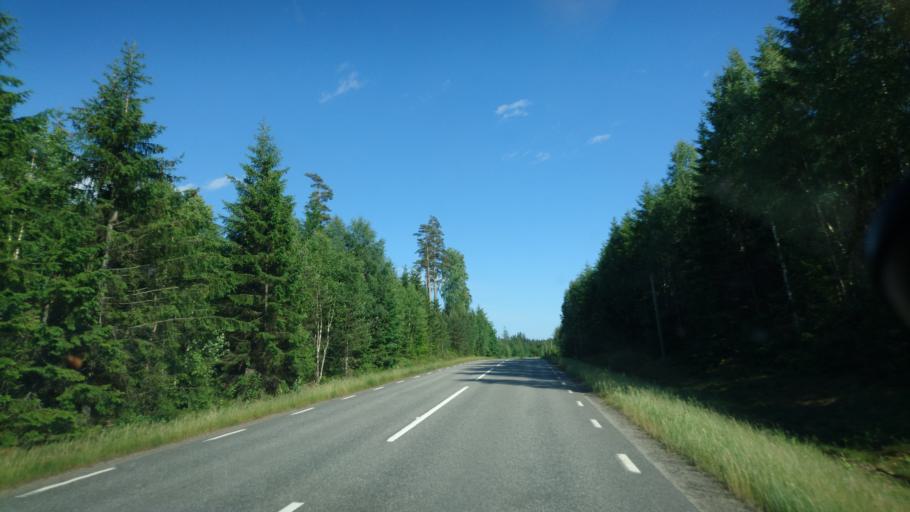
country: SE
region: Skane
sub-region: Osby Kommun
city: Lonsboda
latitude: 56.4259
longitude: 14.2761
